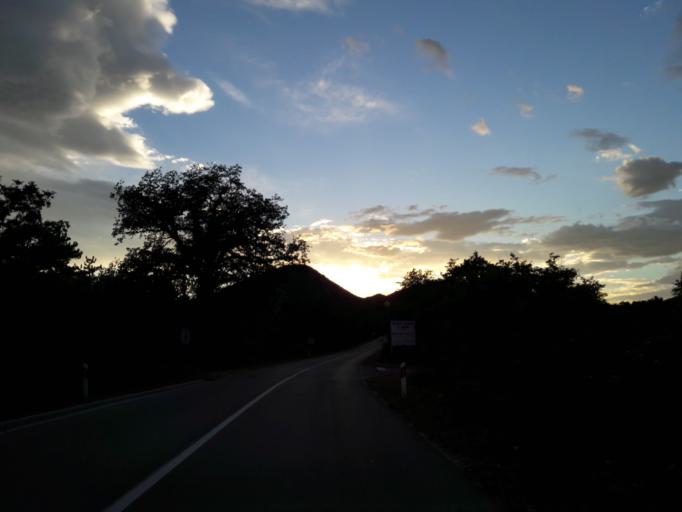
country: HR
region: Dubrovacko-Neretvanska
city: Orebic
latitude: 42.9678
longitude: 17.3031
